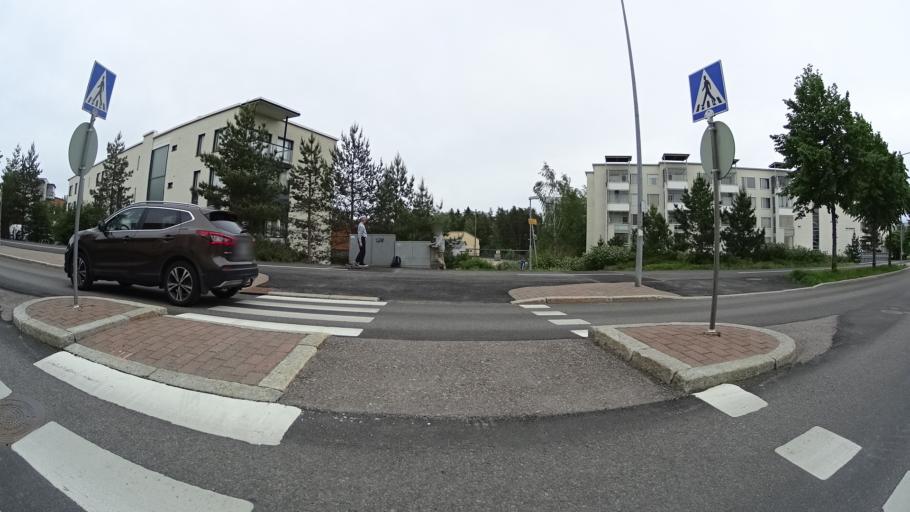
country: FI
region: Uusimaa
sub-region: Helsinki
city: Vantaa
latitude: 60.2449
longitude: 25.0743
